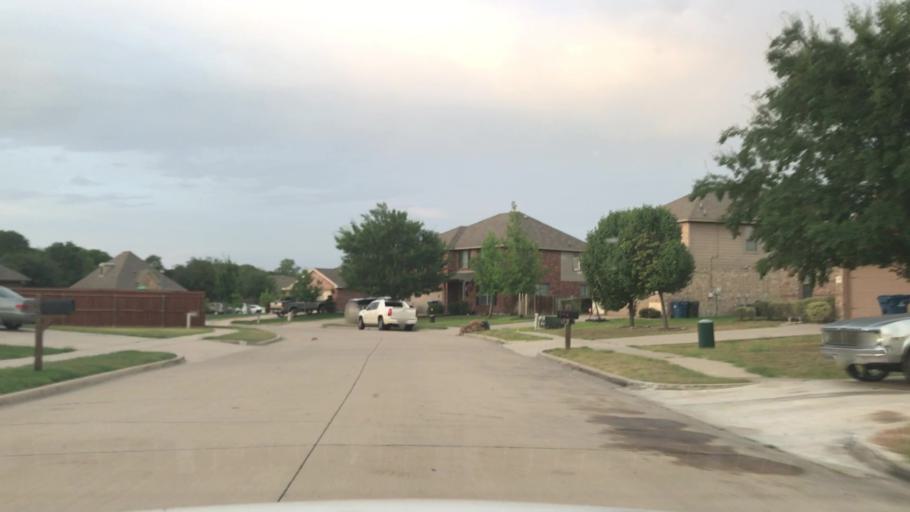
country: US
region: Texas
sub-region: Dallas County
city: Seagoville
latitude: 32.6916
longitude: -96.5523
